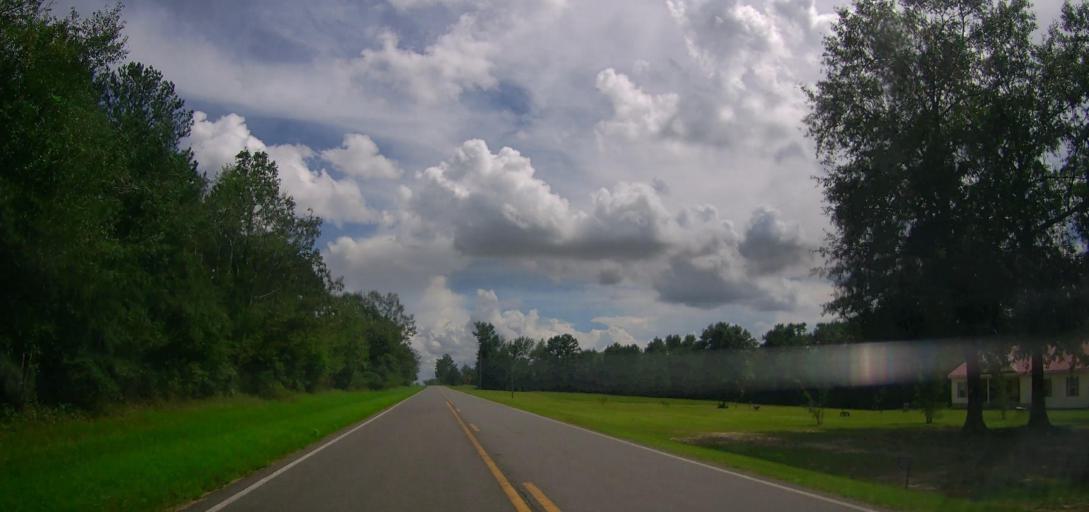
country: US
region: Georgia
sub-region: Taylor County
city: Butler
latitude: 32.4765
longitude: -84.2047
